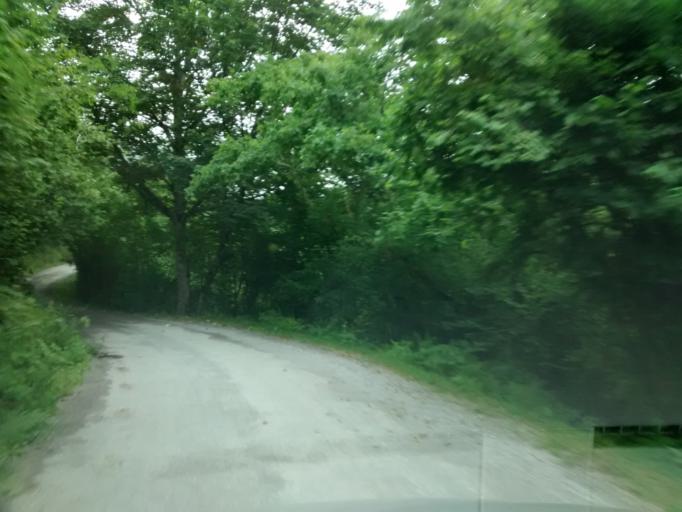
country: ES
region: Asturias
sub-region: Province of Asturias
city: Pilona
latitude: 43.2766
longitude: -5.3494
